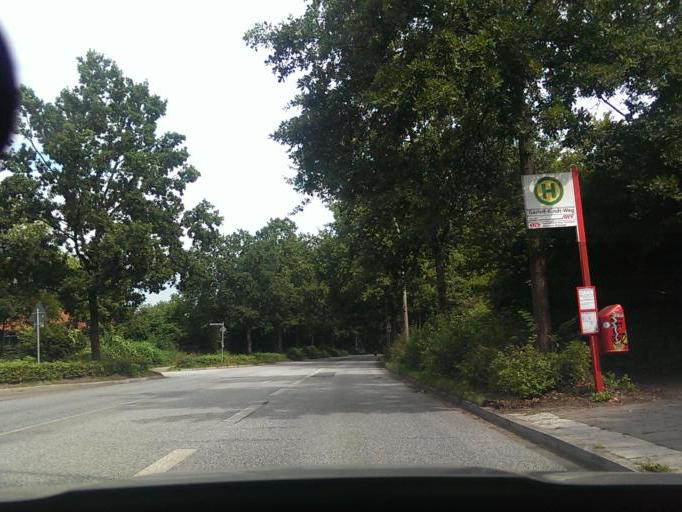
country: DE
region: Hamburg
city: Poppenbuettel
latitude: 53.6658
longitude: 10.0778
